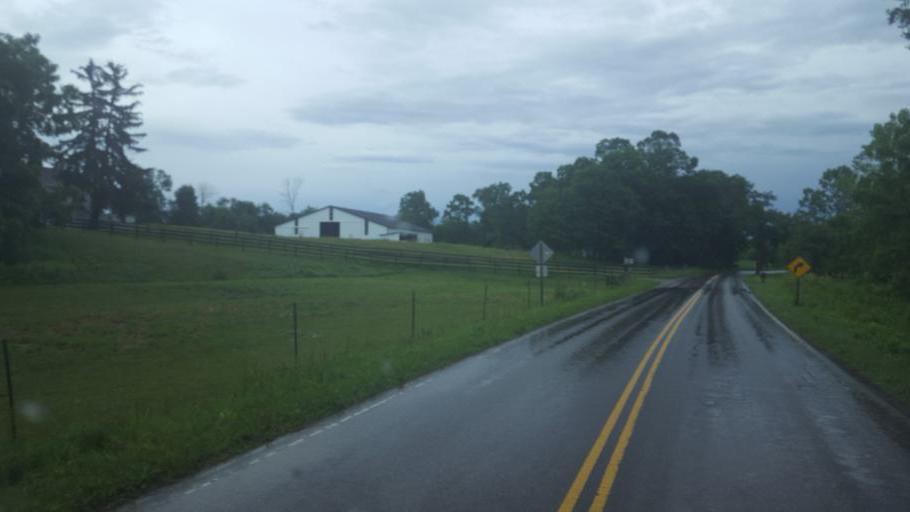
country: US
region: Ohio
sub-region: Knox County
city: Fredericktown
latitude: 40.5427
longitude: -82.6410
